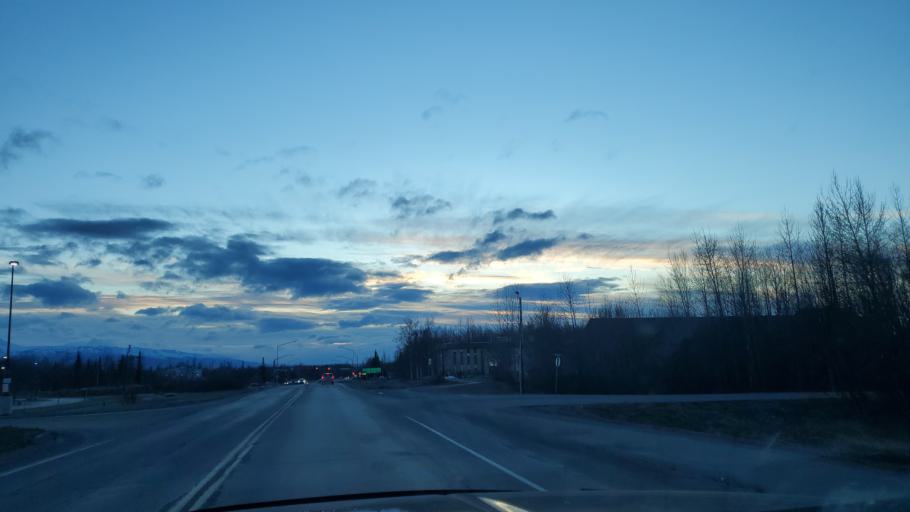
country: US
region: Alaska
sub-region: Matanuska-Susitna Borough
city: Wasilla
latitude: 61.5733
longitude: -149.4427
